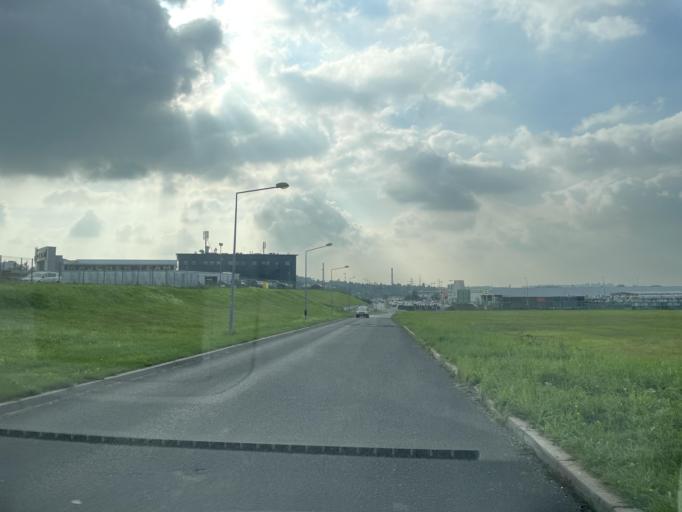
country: PL
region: Silesian Voivodeship
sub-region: Powiat bedzinski
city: Bedzin
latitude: 50.3014
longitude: 19.1696
